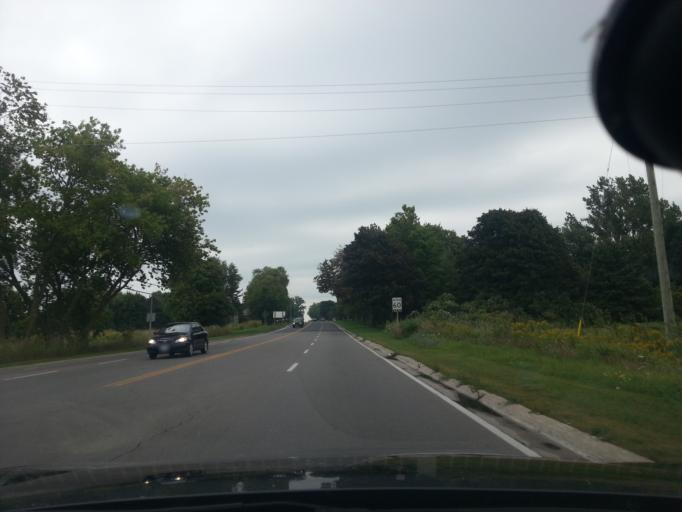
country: CA
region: Ontario
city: Picton
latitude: 43.9951
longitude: -77.1760
